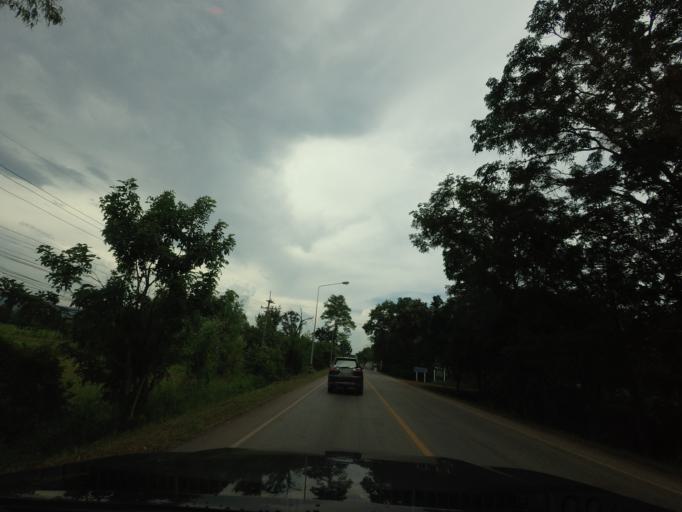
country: TH
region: Khon Kaen
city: Nong Na Kham
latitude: 16.8136
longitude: 102.3334
